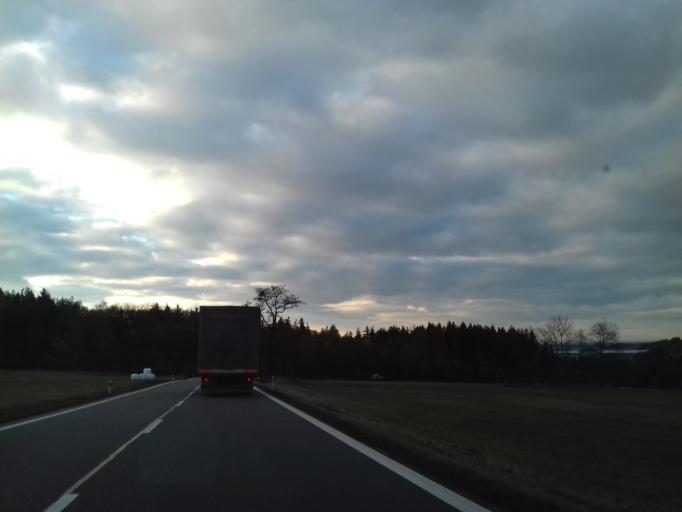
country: CZ
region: Pardubicky
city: Krouna
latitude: 49.7663
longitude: 16.0784
